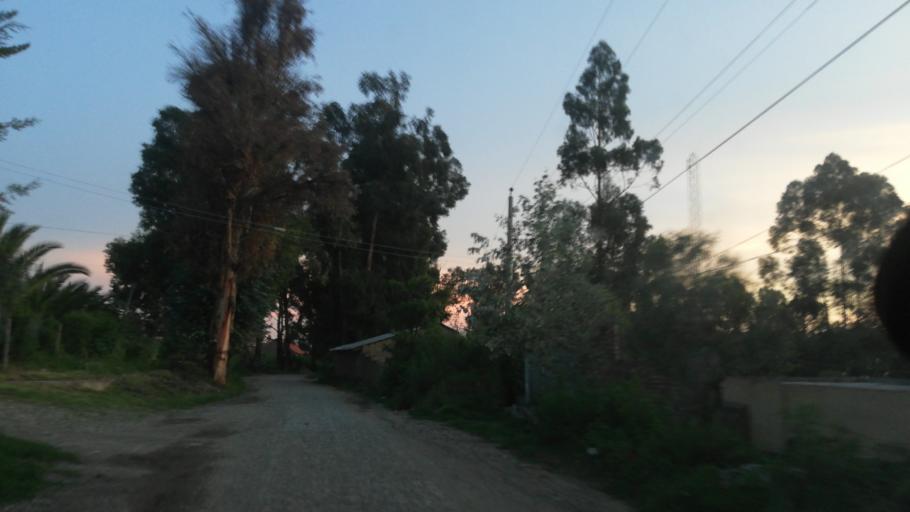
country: BO
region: Cochabamba
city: Cochabamba
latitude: -17.3223
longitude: -66.2090
